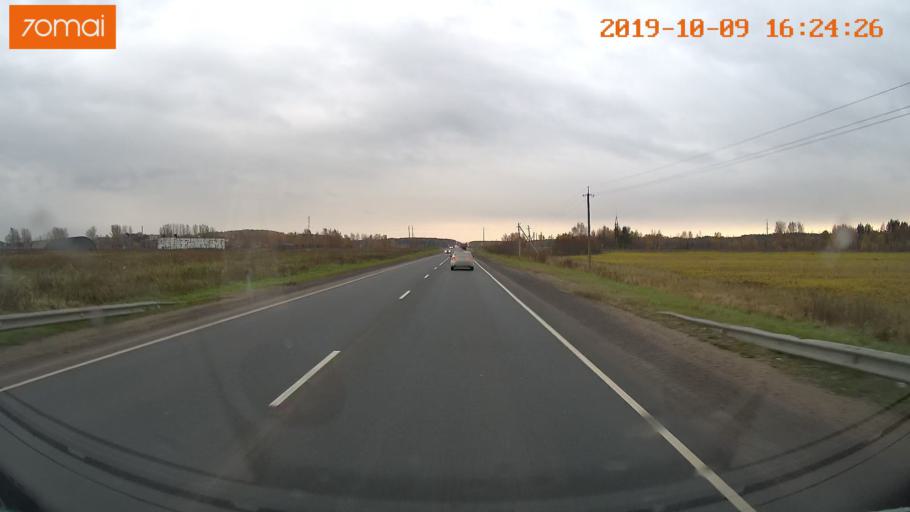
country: RU
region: Kostroma
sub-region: Kostromskoy Rayon
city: Kostroma
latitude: 57.6525
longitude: 40.9103
